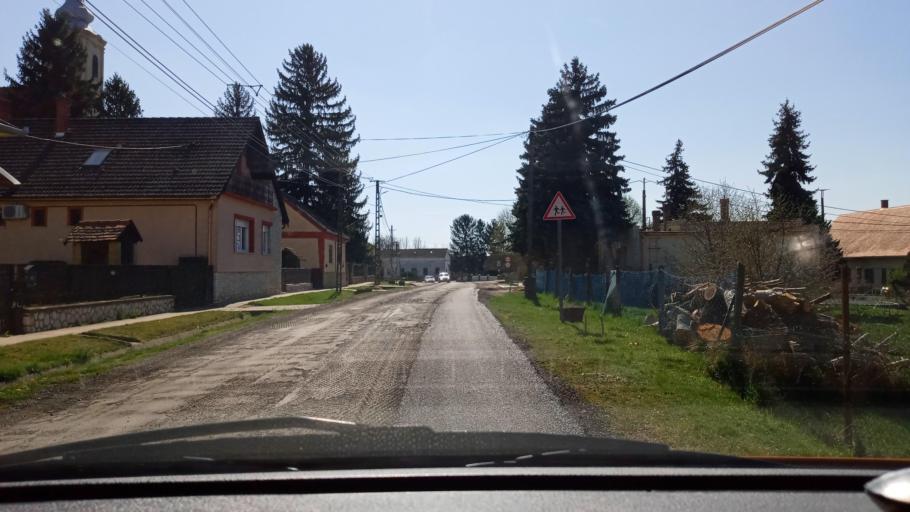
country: HU
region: Baranya
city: Boly
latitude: 46.0088
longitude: 18.4162
